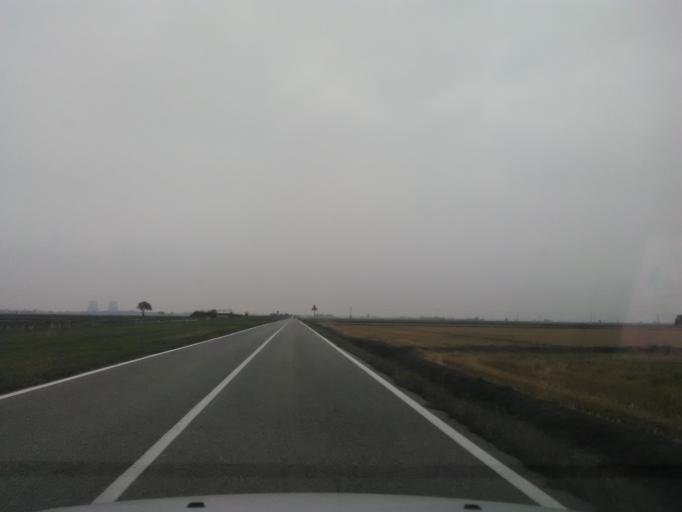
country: IT
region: Piedmont
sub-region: Provincia di Vercelli
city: Bianze
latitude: 45.2689
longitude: 8.1366
